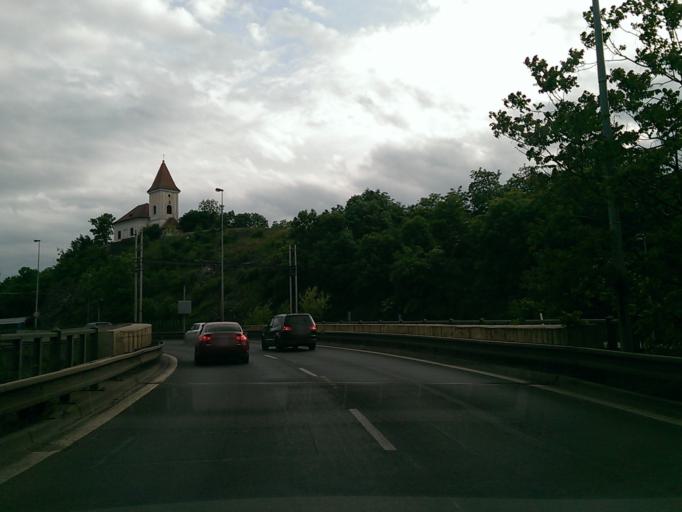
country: CZ
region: Praha
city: Branik
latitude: 50.0488
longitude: 14.4100
